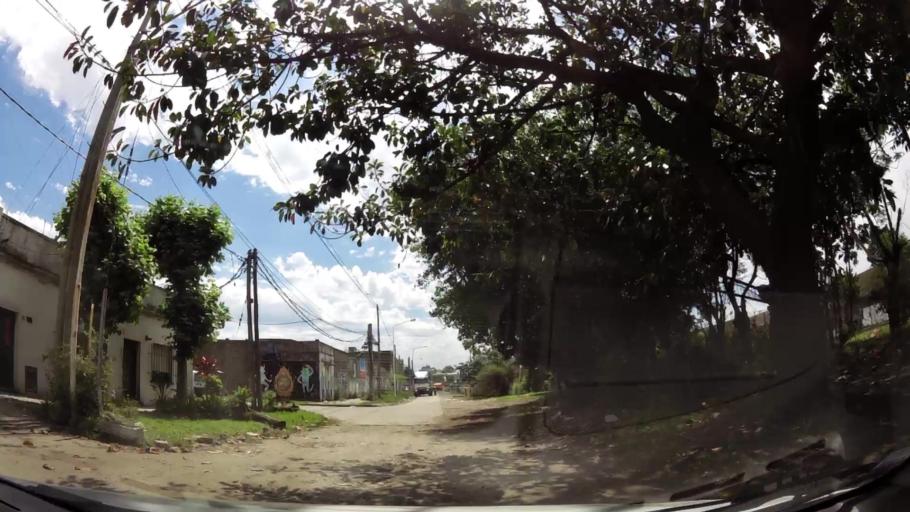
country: AR
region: Buenos Aires
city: San Justo
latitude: -34.6798
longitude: -58.5461
